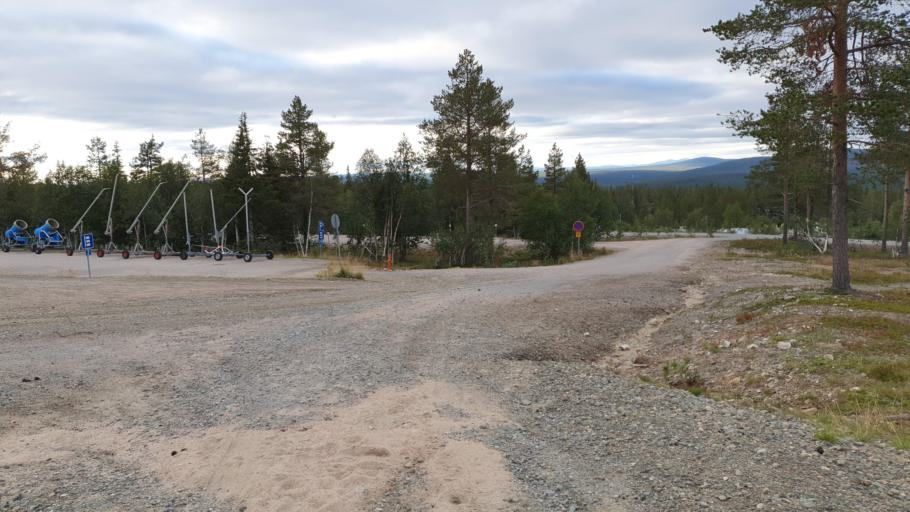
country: FI
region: Lapland
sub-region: Tunturi-Lappi
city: Kolari
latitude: 67.5804
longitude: 24.2049
